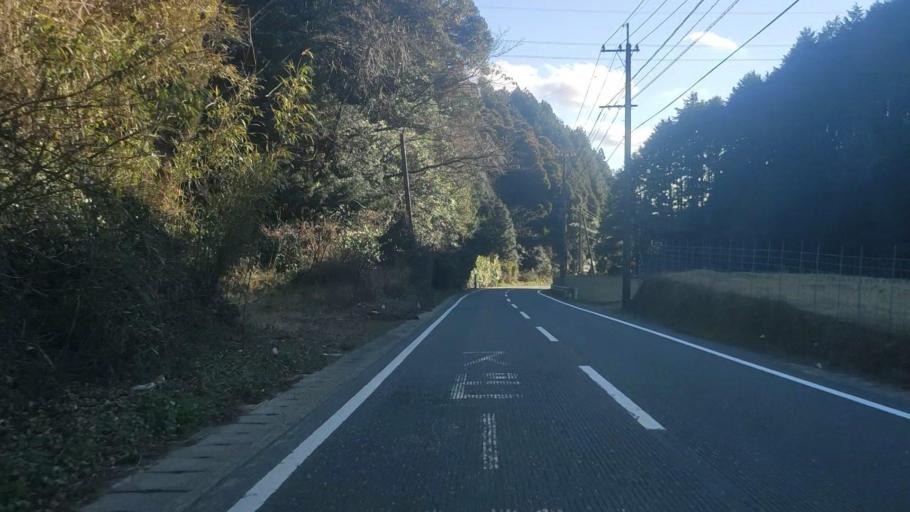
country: JP
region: Saga Prefecture
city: Kanzakimachi-kanzaki
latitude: 33.3980
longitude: 130.2717
